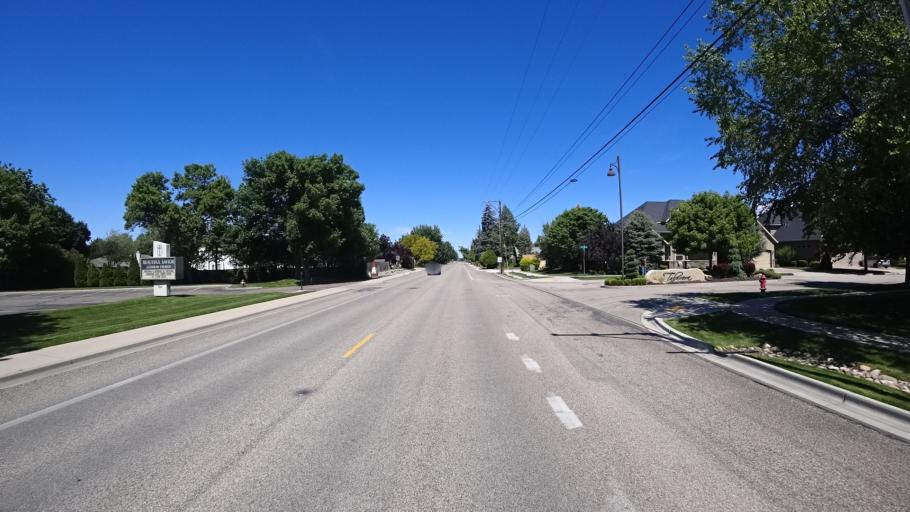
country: US
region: Idaho
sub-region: Ada County
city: Boise
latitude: 43.5653
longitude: -116.1457
